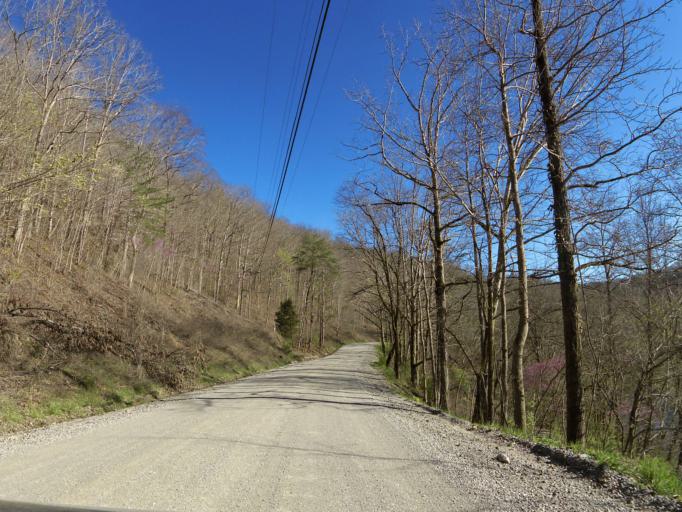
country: US
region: Tennessee
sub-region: Scott County
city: Huntsville
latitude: 36.3104
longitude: -84.3814
